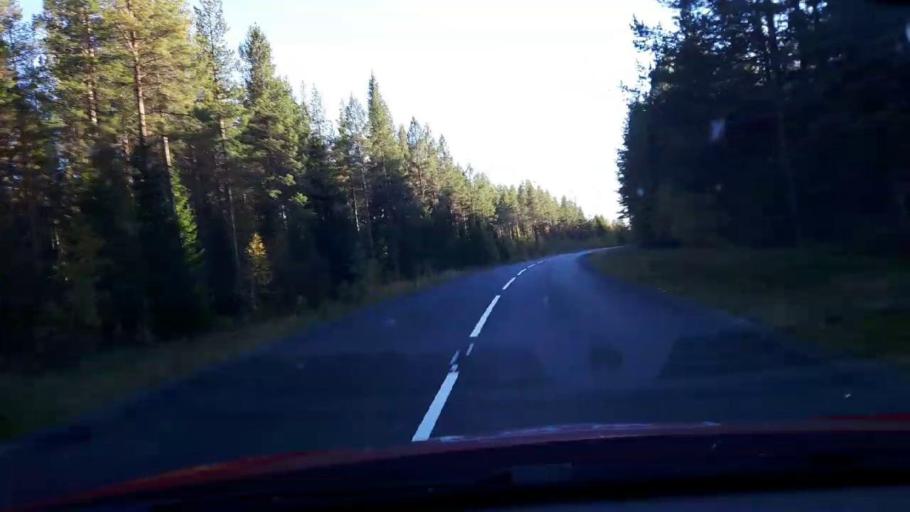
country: SE
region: Jaemtland
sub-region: OEstersunds Kommun
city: Lit
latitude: 63.4698
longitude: 14.8766
